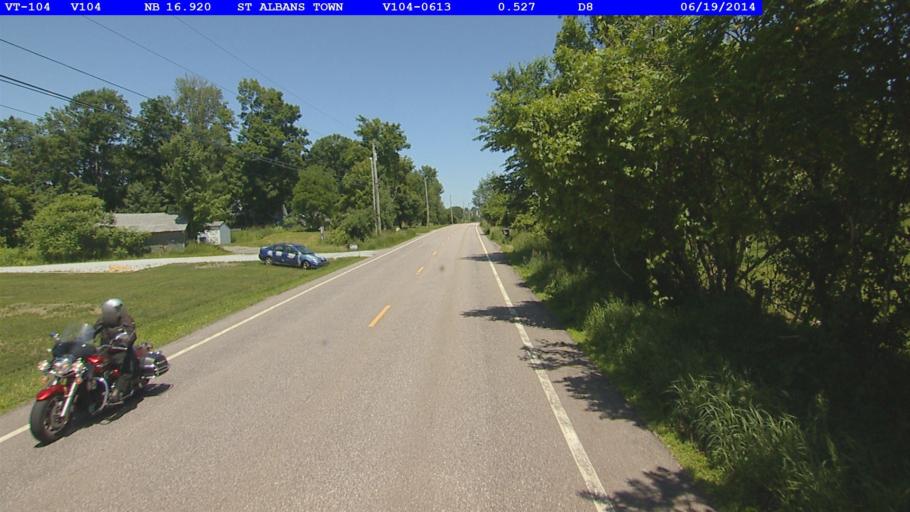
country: US
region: Vermont
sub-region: Franklin County
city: Saint Albans
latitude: 44.7813
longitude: -73.0785
